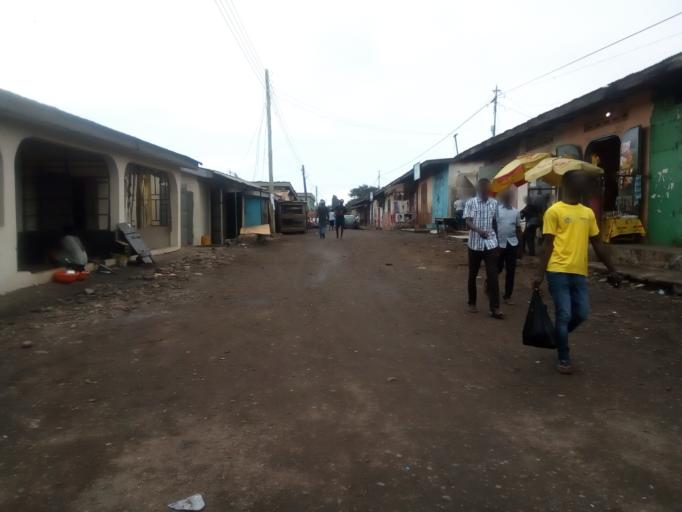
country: GH
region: Greater Accra
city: Dome
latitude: 5.6085
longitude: -0.2560
